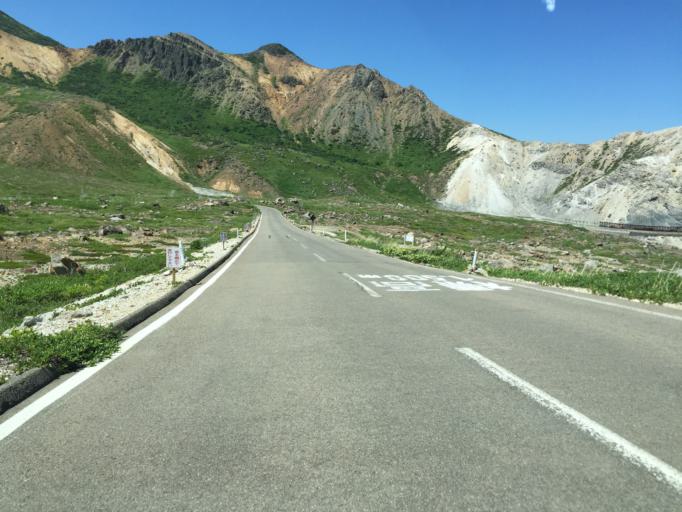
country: JP
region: Fukushima
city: Fukushima-shi
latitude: 37.7277
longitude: 140.2596
